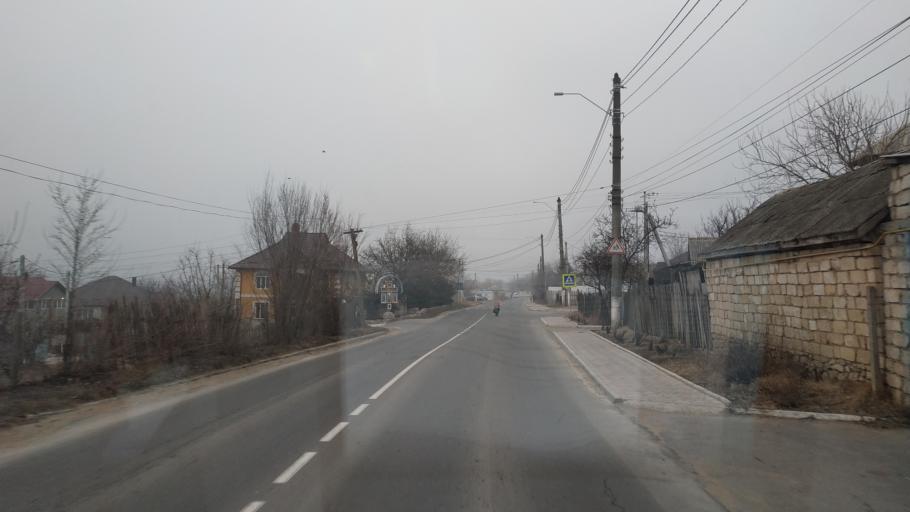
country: MD
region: Laloveni
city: Ialoveni
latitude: 46.9401
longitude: 28.7880
